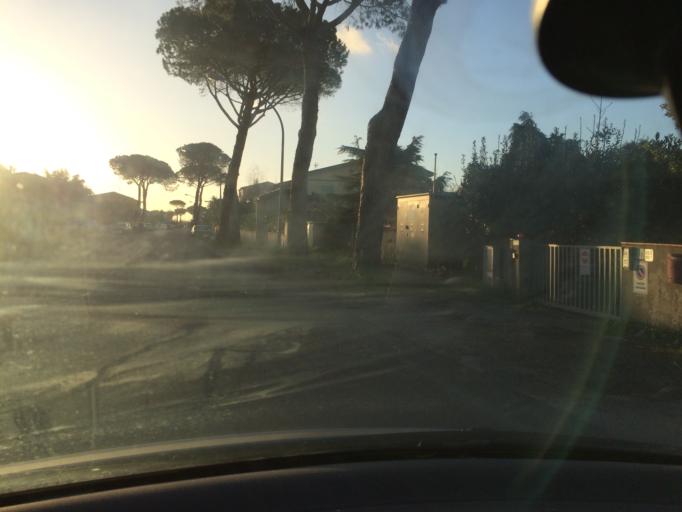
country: IT
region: Tuscany
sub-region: Province of Pisa
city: Gello
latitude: 43.7222
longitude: 10.4402
